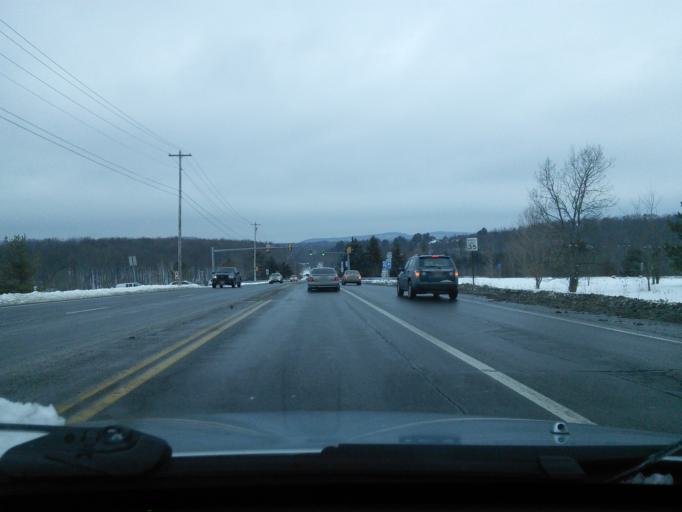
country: US
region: Pennsylvania
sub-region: Centre County
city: Park Forest Village
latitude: 40.8171
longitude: -77.8999
